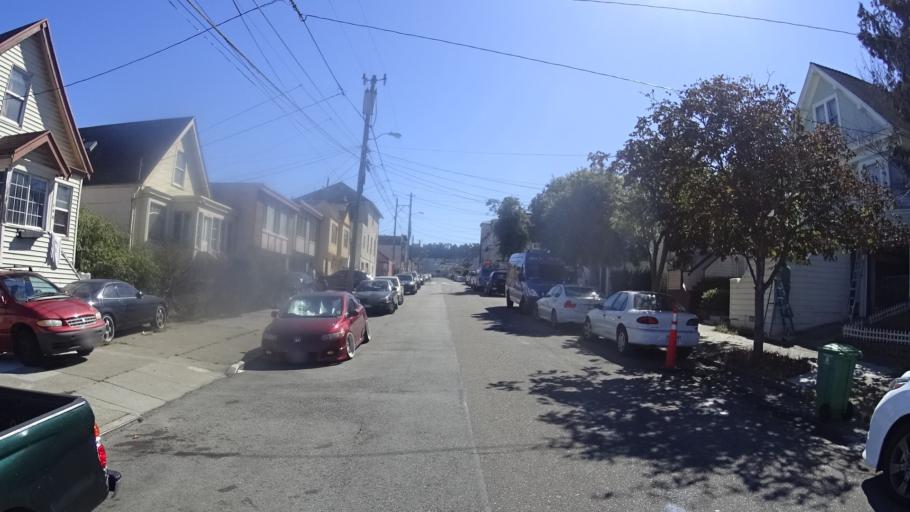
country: US
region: California
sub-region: San Mateo County
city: Daly City
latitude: 37.7090
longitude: -122.4596
